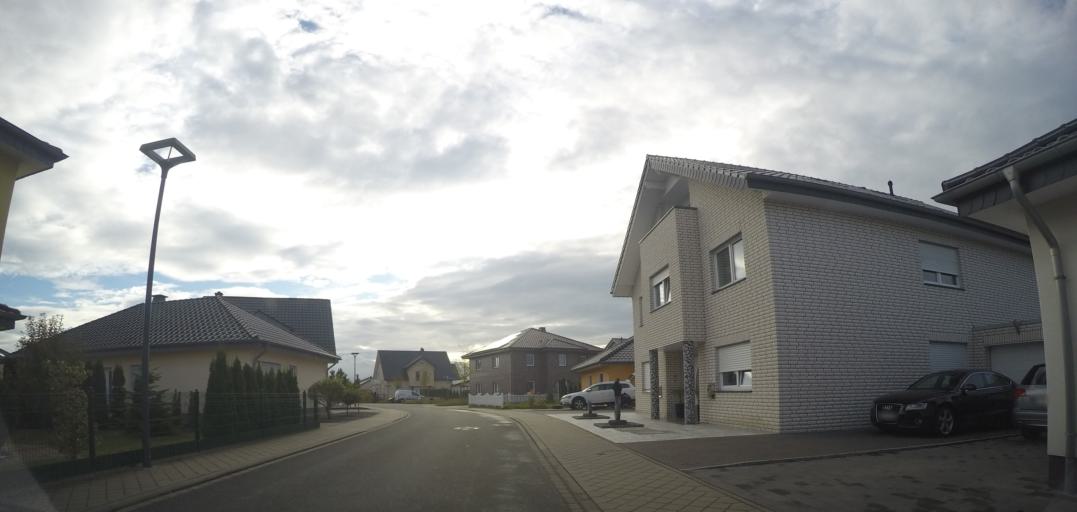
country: DE
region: North Rhine-Westphalia
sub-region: Regierungsbezirk Arnsberg
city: Lippstadt
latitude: 51.6566
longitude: 8.3346
